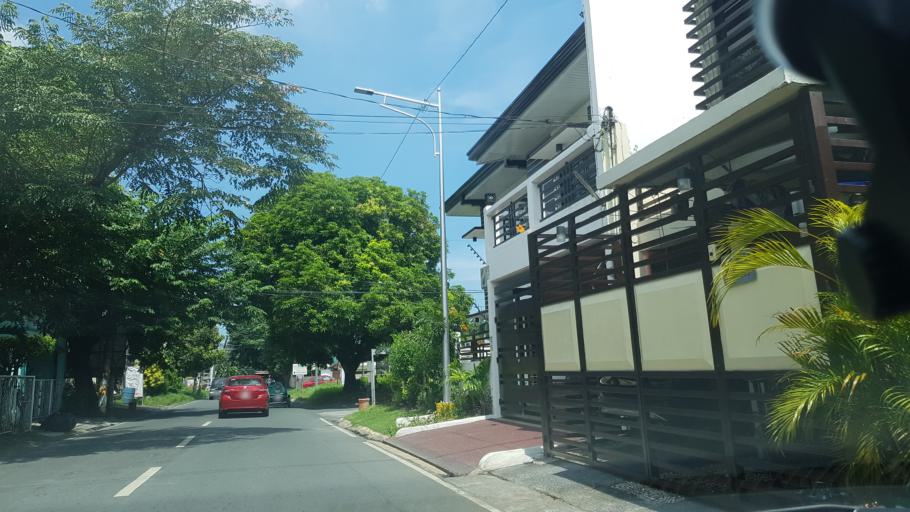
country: PH
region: Calabarzon
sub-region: Province of Rizal
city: Las Pinas
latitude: 14.4360
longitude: 120.9922
